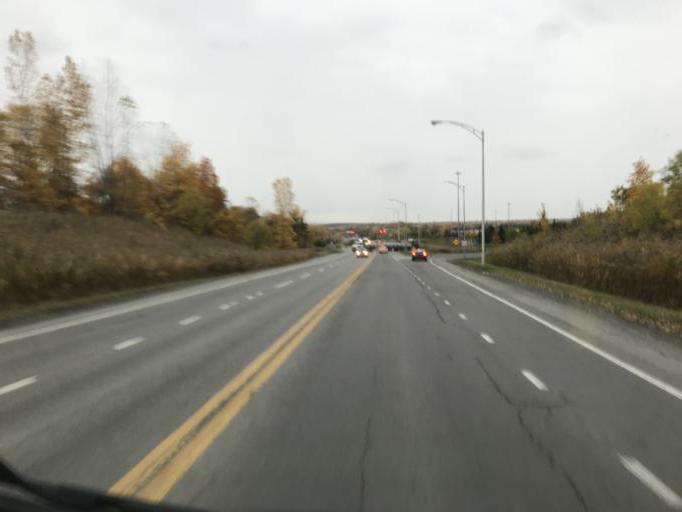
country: CA
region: Quebec
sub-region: Lanaudiere
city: Lorraine
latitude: 45.6756
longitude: -73.7674
